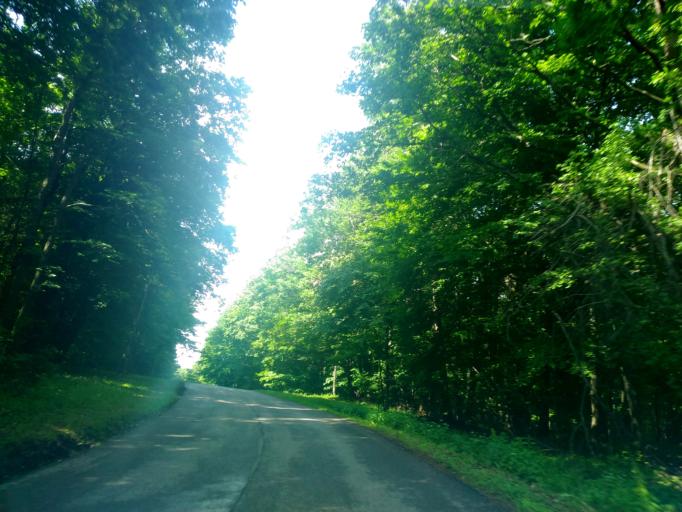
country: HU
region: Baranya
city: Pecs
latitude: 46.1267
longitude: 18.2268
